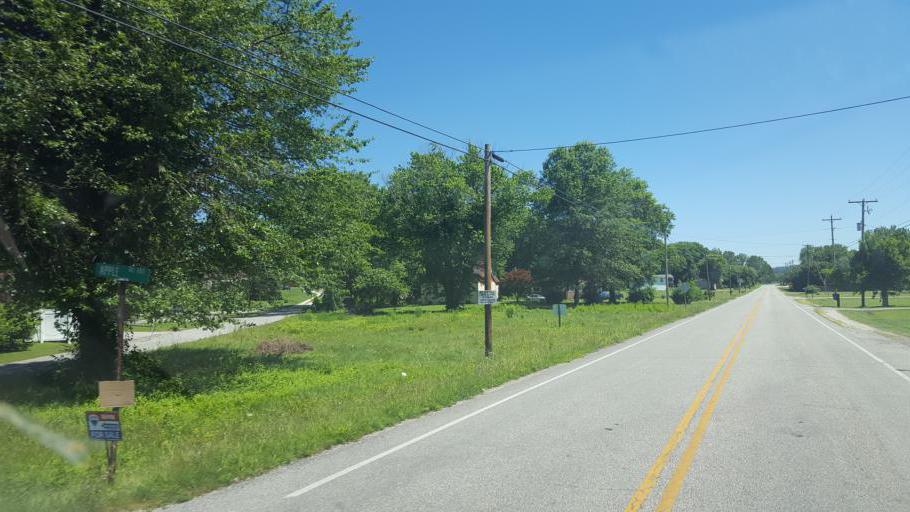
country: US
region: West Virginia
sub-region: Cabell County
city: Pea Ridge
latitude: 38.4468
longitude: -82.3323
